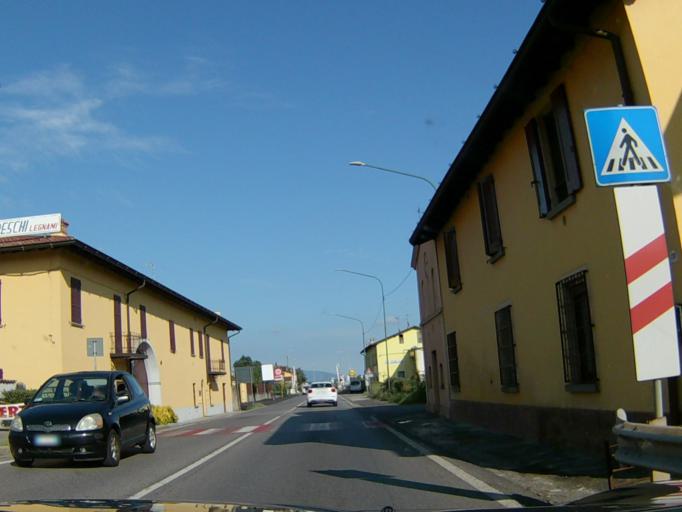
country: IT
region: Lombardy
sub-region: Provincia di Brescia
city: Rovato
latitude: 45.5612
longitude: 10.0010
